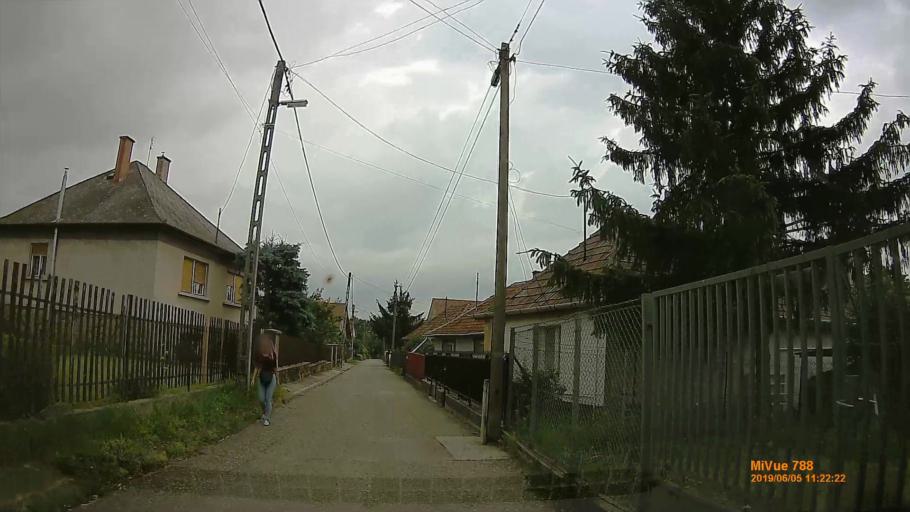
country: HU
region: Pest
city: Maglod
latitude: 47.4402
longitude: 19.3456
